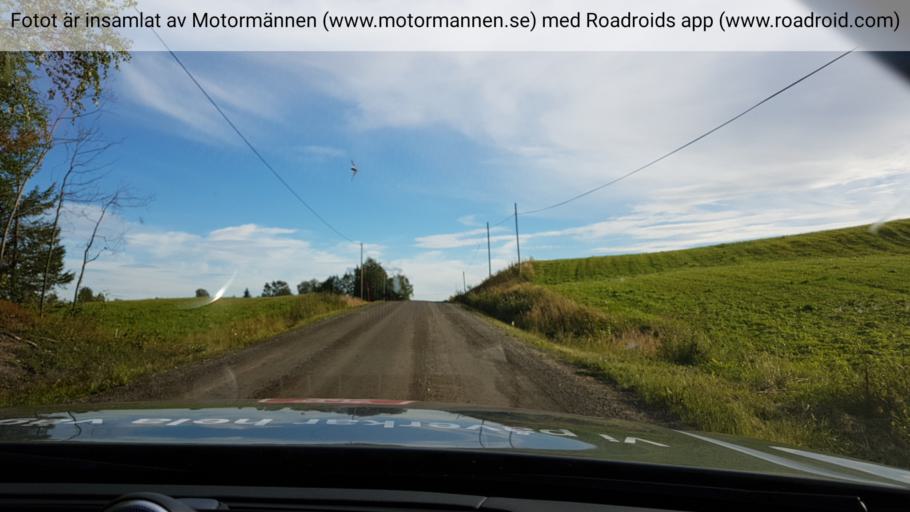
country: SE
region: Jaemtland
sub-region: Stroemsunds Kommun
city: Stroemsund
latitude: 64.0513
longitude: 15.8113
